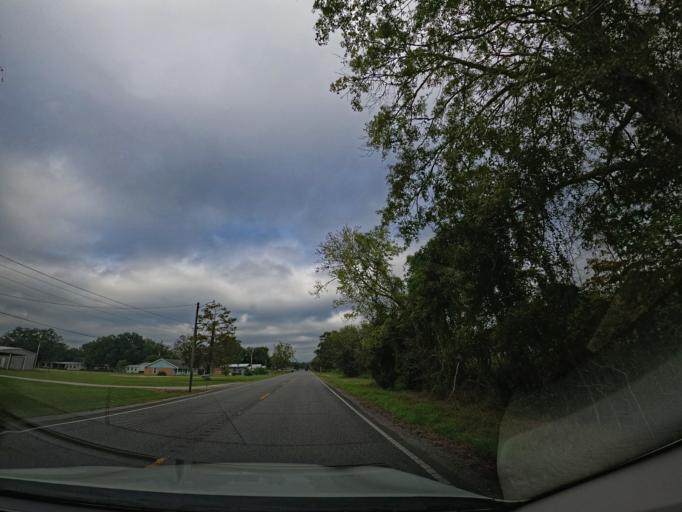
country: US
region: Louisiana
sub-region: Saint Mary Parish
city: Amelia
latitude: 29.6388
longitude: -90.9544
